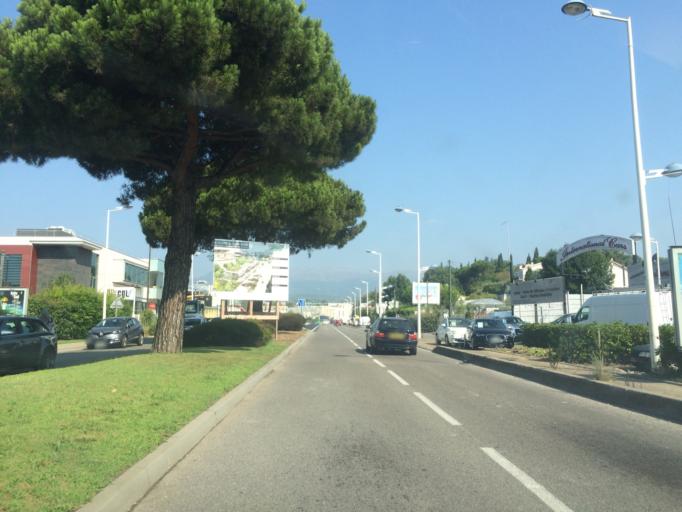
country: FR
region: Provence-Alpes-Cote d'Azur
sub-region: Departement des Alpes-Maritimes
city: Villeneuve-Loubet
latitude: 43.6633
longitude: 7.1311
